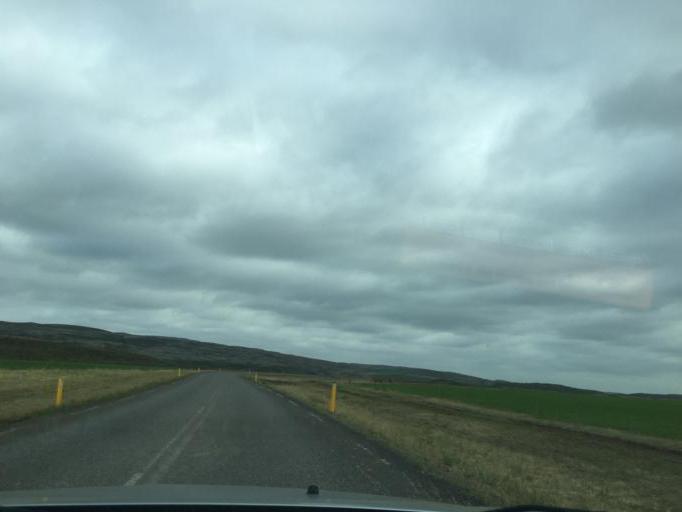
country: IS
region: South
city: Vestmannaeyjar
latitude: 64.2741
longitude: -20.2267
